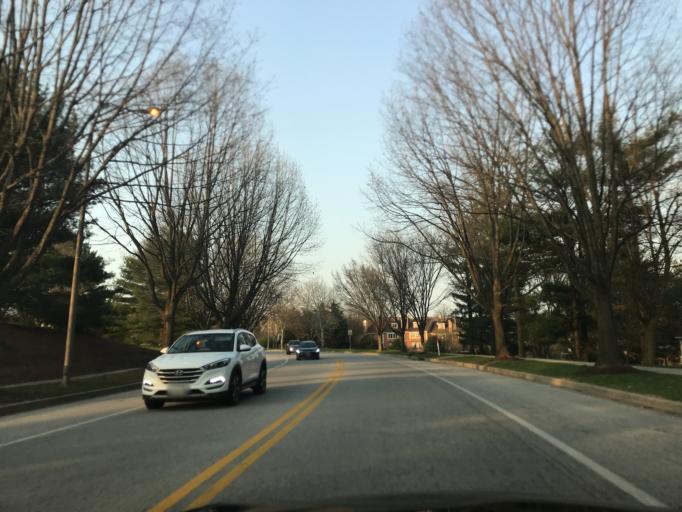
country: US
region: Maryland
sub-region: Howard County
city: Columbia
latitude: 39.2346
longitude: -76.8447
